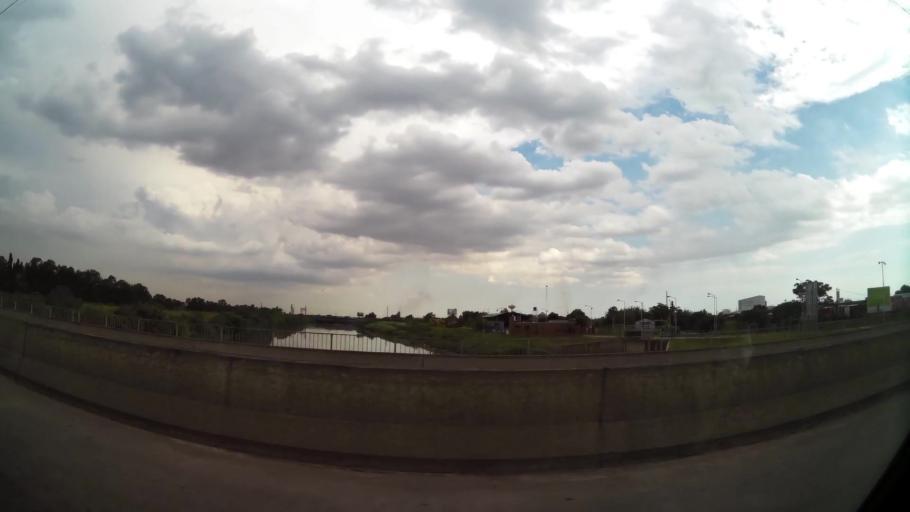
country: AR
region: Buenos Aires
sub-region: Partido de Tigre
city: Tigre
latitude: -34.4804
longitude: -58.6038
